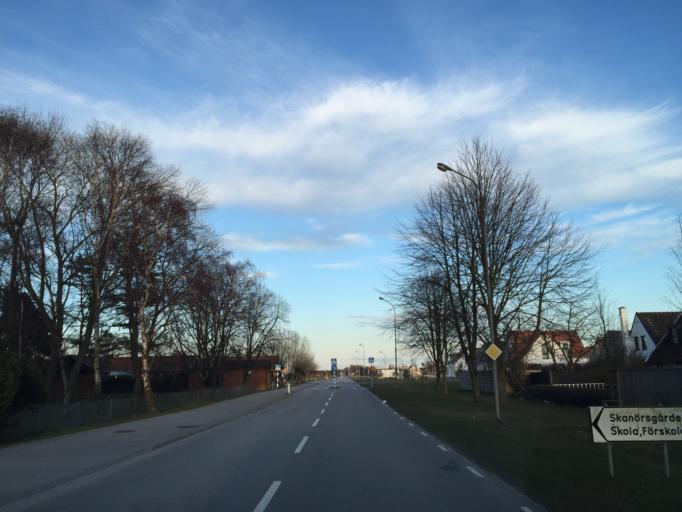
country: SE
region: Skane
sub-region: Vellinge Kommun
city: Skanor med Falsterbo
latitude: 55.4163
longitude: 12.8587
